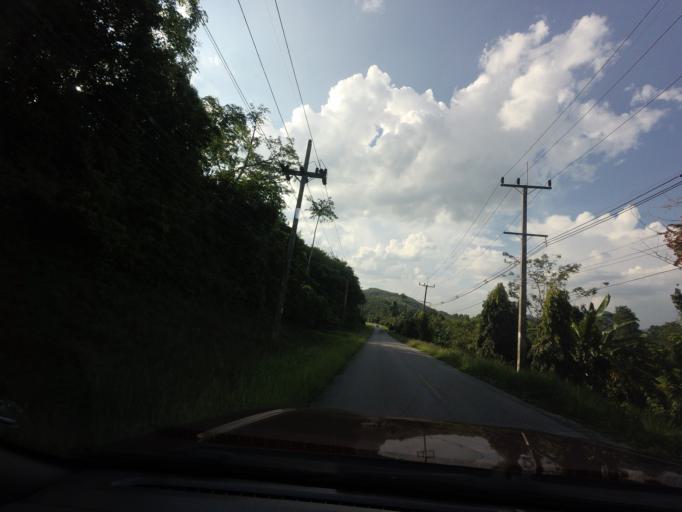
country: TH
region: Yala
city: Ban Nang Sata
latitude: 6.1935
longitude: 101.2597
